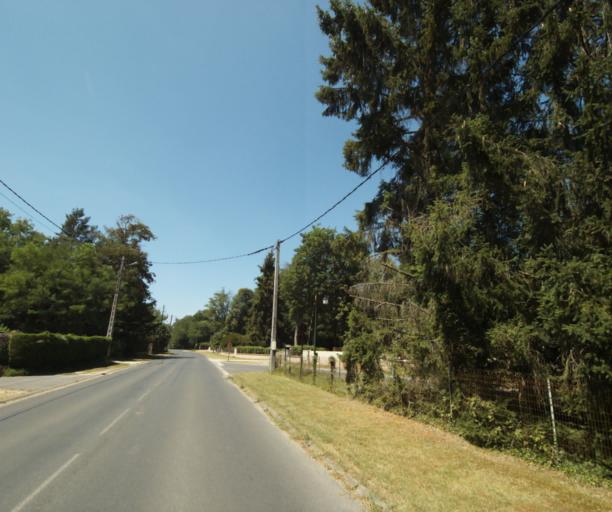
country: FR
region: Ile-de-France
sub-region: Departement de Seine-et-Marne
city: Noisy-sur-Ecole
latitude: 48.3633
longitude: 2.5197
